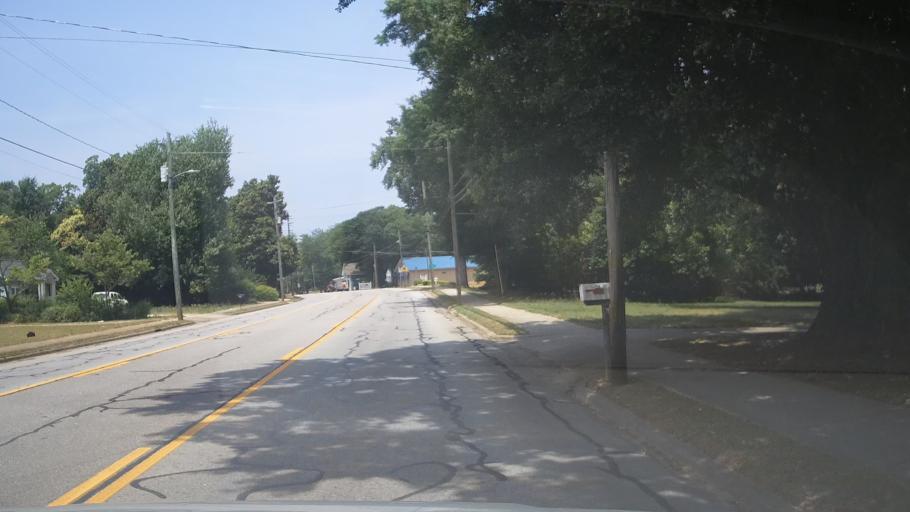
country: US
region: Georgia
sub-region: Hart County
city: Hartwell
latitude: 34.3462
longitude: -82.9268
